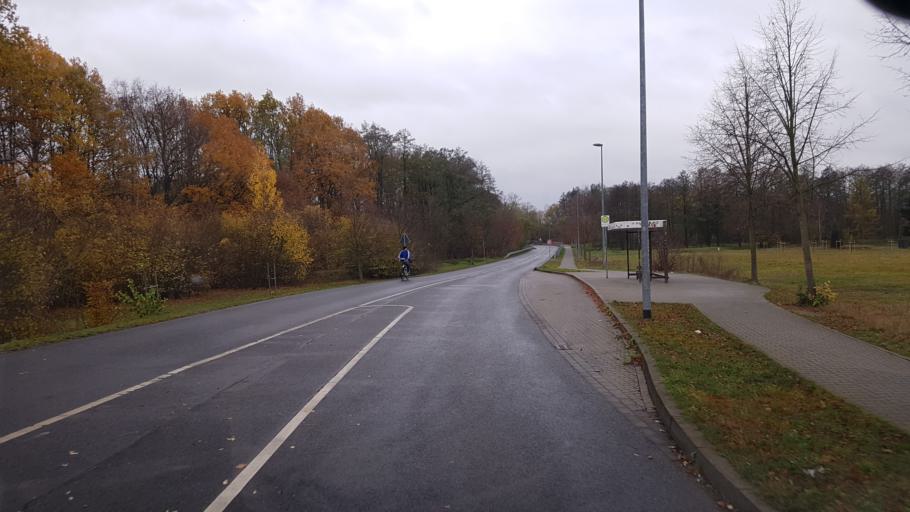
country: DE
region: Brandenburg
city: Ortrand
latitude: 51.3783
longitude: 13.7682
